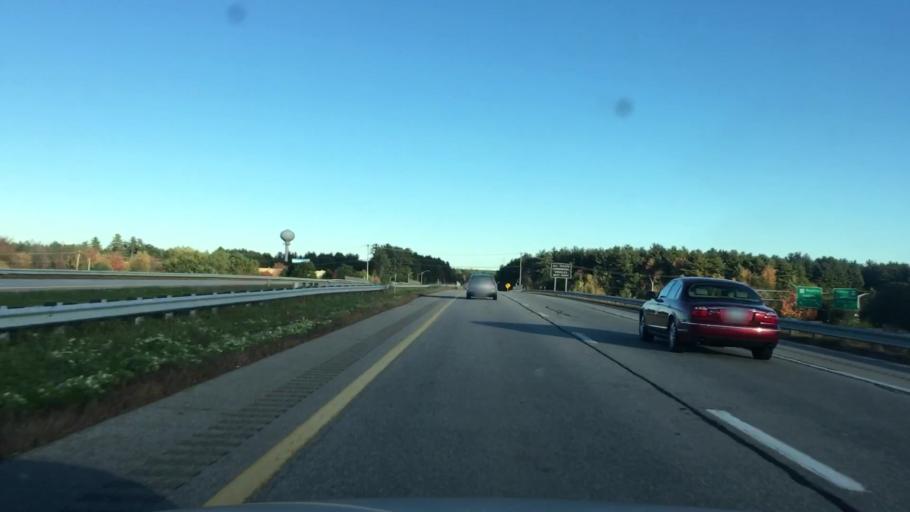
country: US
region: New Hampshire
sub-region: Rockingham County
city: Epping
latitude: 43.0267
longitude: -71.0762
